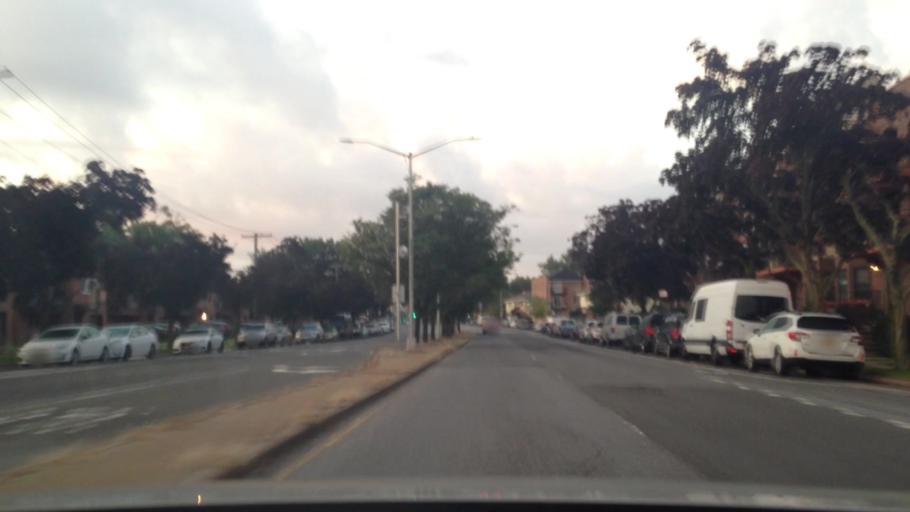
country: US
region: New York
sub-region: Queens County
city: Jamaica
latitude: 40.7303
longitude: -73.8052
